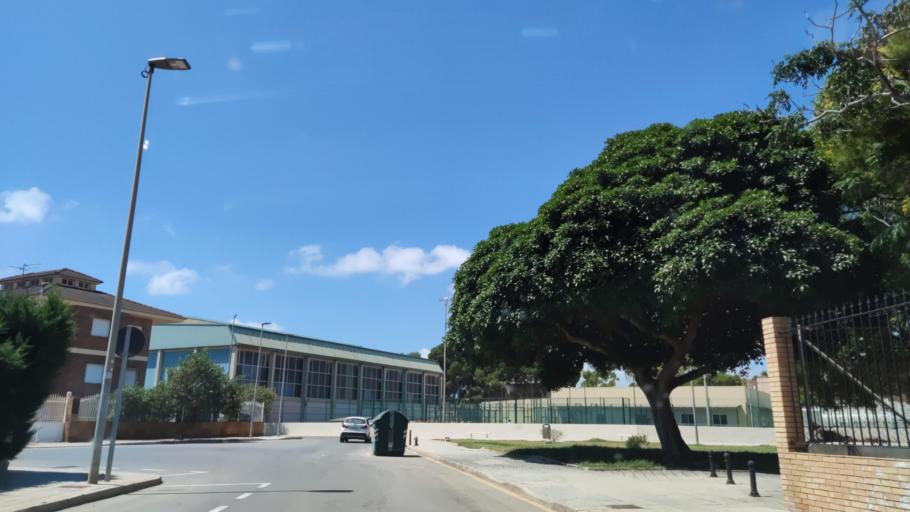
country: ES
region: Murcia
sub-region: Murcia
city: Los Alcazares
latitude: 37.7552
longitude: -0.8377
